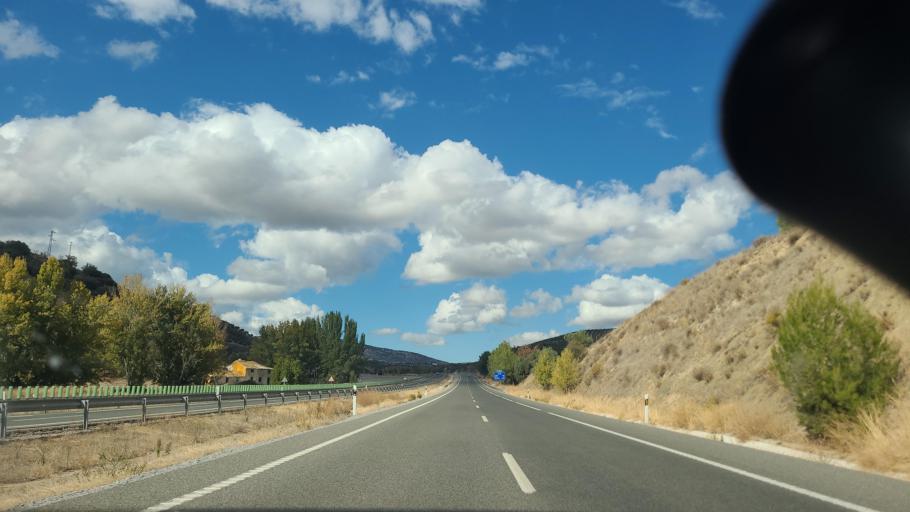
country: ES
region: Andalusia
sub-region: Provincia de Granada
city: Campotejar
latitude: 37.5012
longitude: -3.6283
